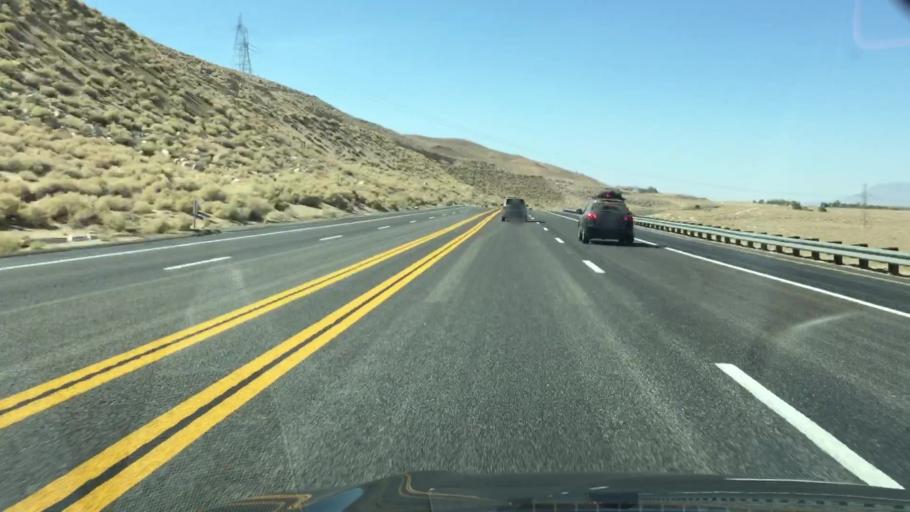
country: US
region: California
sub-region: Inyo County
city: Lone Pine
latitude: 36.5220
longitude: -118.0414
